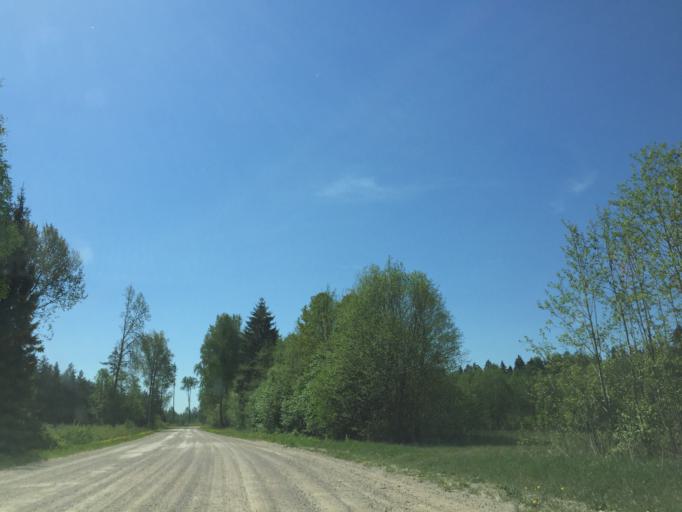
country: LV
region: Kegums
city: Kegums
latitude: 56.8884
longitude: 24.7898
